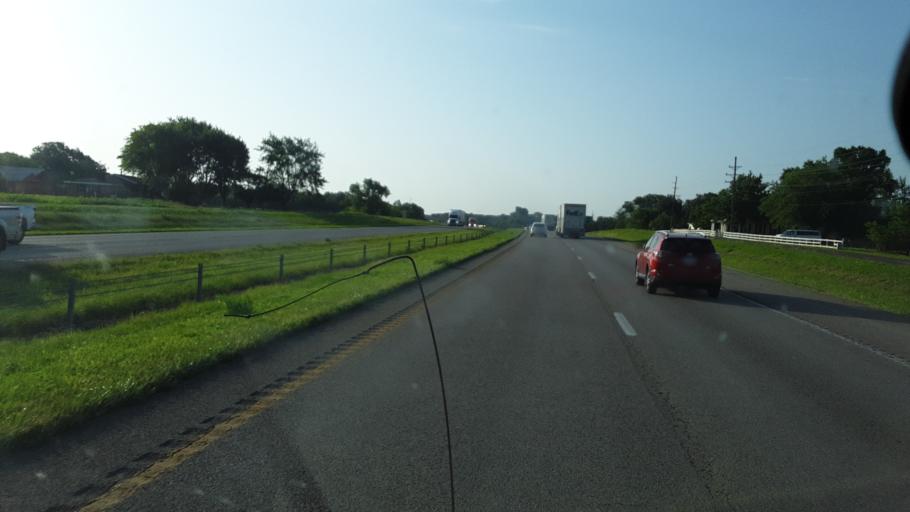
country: US
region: Missouri
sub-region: Warren County
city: Warrenton
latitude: 38.8305
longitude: -91.2152
